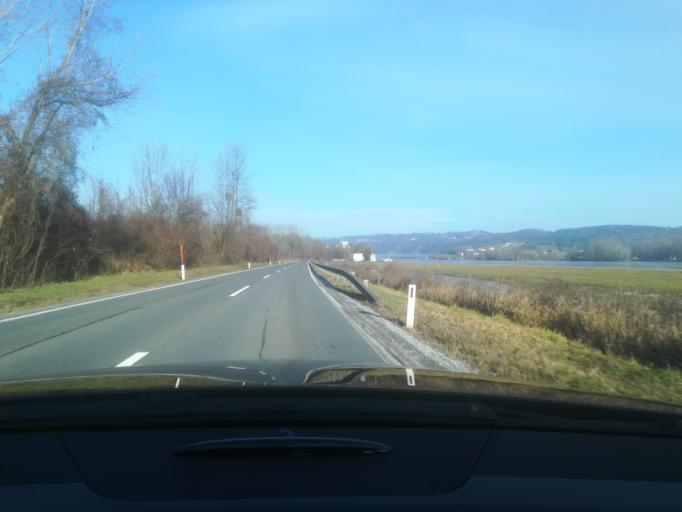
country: AT
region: Upper Austria
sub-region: Politischer Bezirk Urfahr-Umgebung
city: Feldkirchen an der Donau
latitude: 48.3464
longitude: 14.0186
